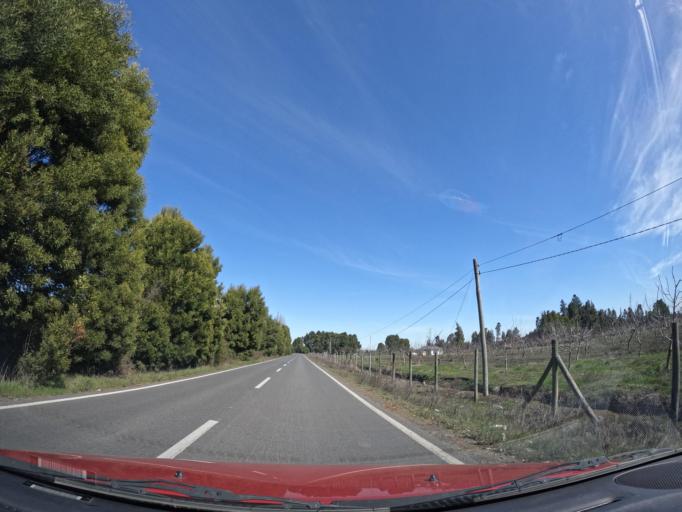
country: CL
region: Biobio
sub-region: Provincia de Biobio
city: Cabrero
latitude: -37.0341
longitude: -72.3714
